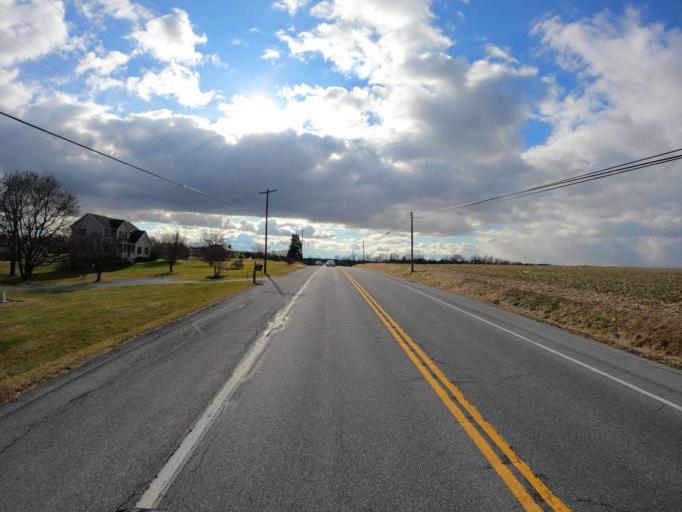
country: US
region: Maryland
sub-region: Frederick County
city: Linganore
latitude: 39.4723
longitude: -77.2720
